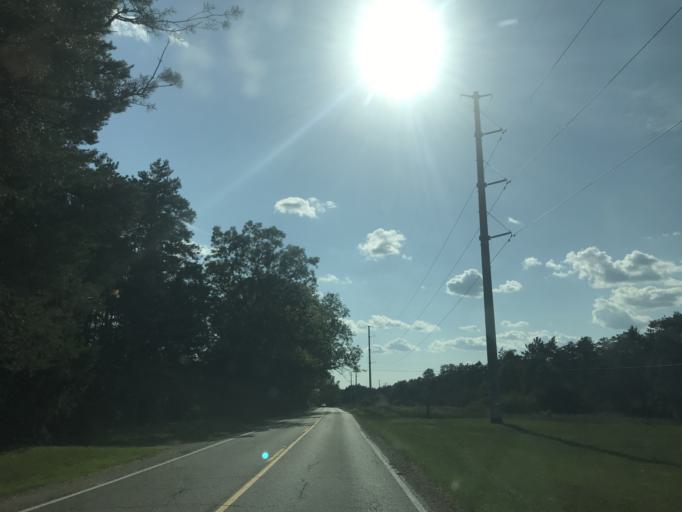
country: US
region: Michigan
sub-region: Newaygo County
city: Newaygo
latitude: 43.4288
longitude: -85.7541
